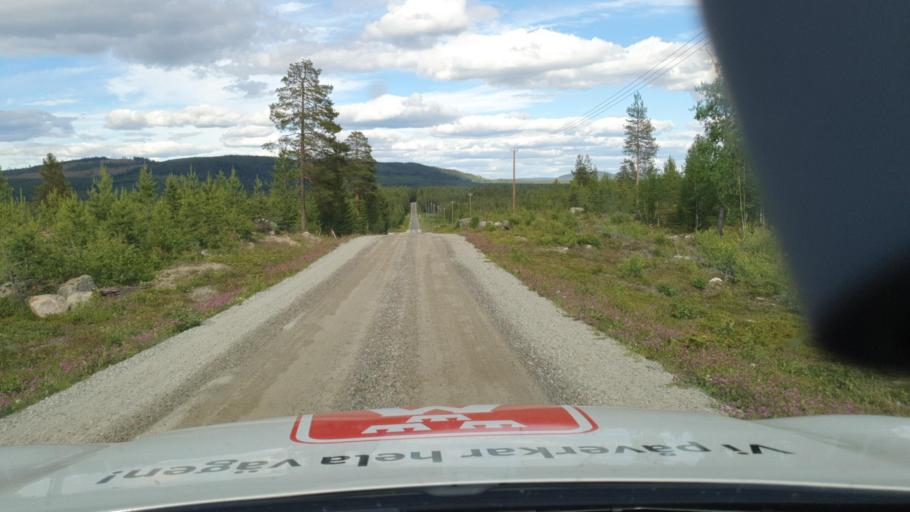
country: SE
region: Vaesterbotten
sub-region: Asele Kommun
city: Insjon
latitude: 64.2340
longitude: 17.9003
